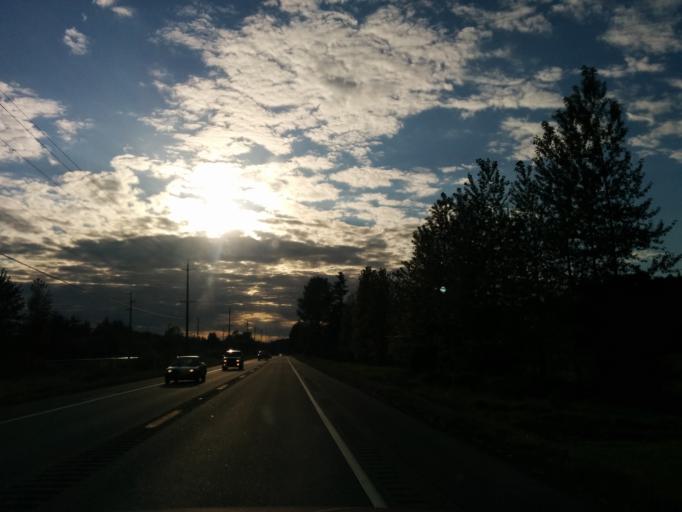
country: US
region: Washington
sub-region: Snohomish County
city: Woods Creek
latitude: 47.8551
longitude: -121.9126
